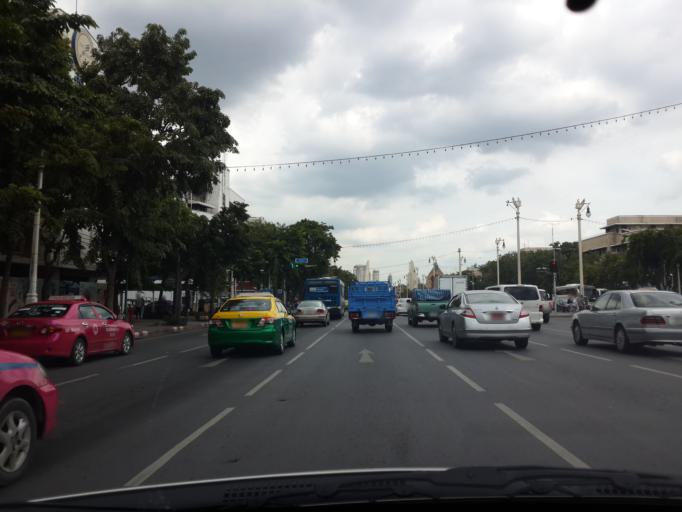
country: TH
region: Bangkok
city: Bangkok
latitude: 13.7576
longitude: 100.4984
